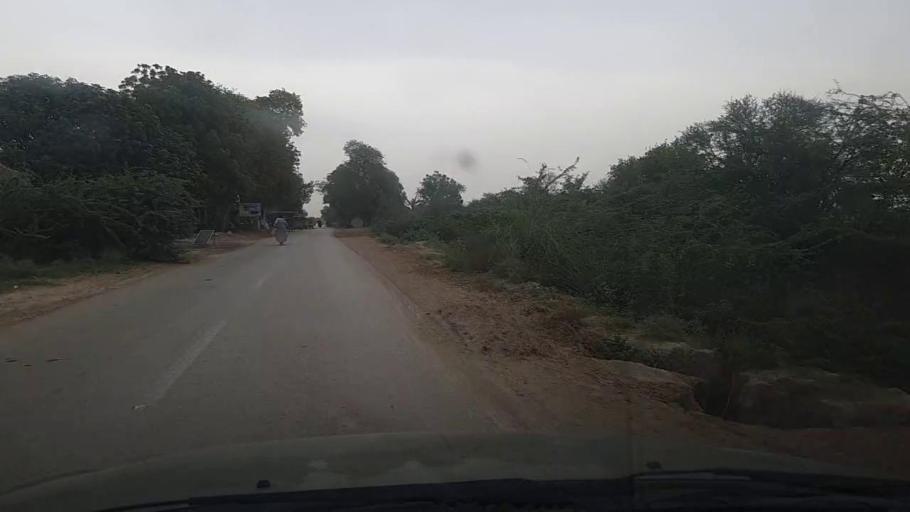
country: PK
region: Sindh
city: Daur
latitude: 26.3458
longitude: 68.1316
